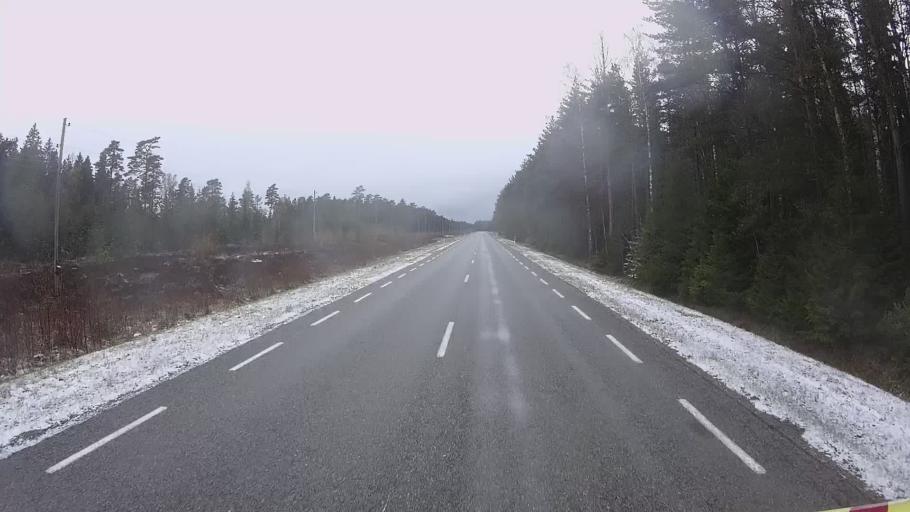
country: EE
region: Hiiumaa
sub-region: Kaerdla linn
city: Kardla
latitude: 59.0186
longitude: 22.6721
